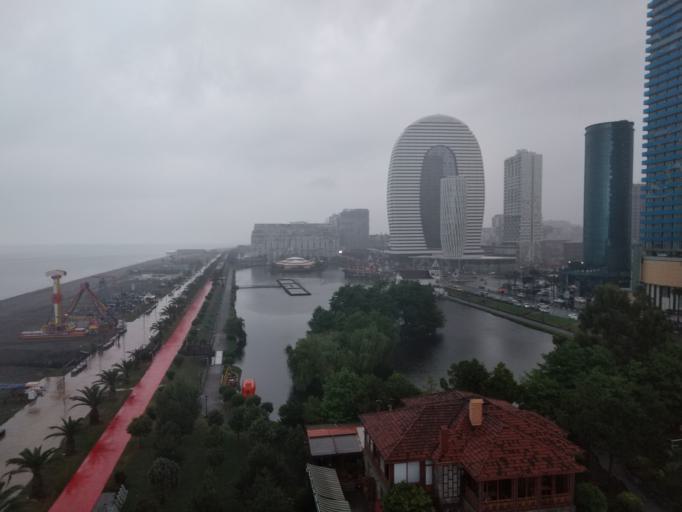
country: GE
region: Ajaria
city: Batumi
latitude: 41.6400
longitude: 41.6113
